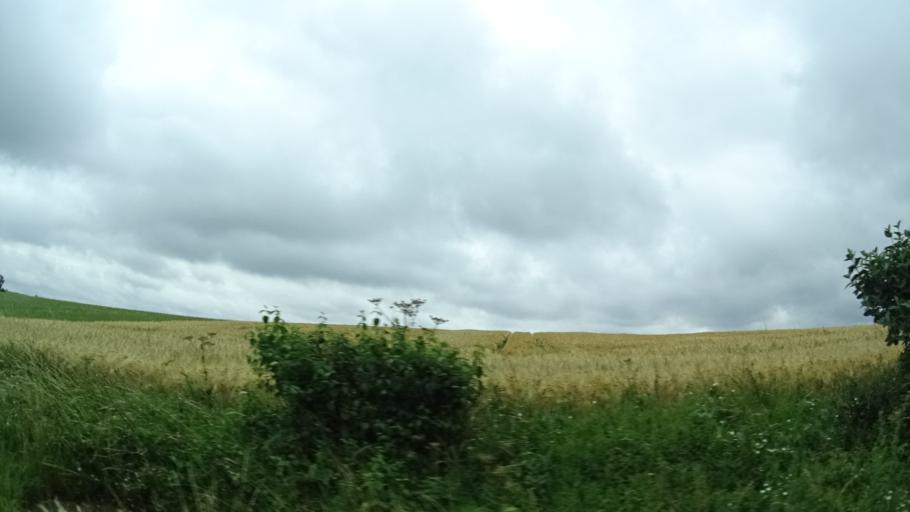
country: LU
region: Luxembourg
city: Schouweiler
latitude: 49.5911
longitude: 5.9621
